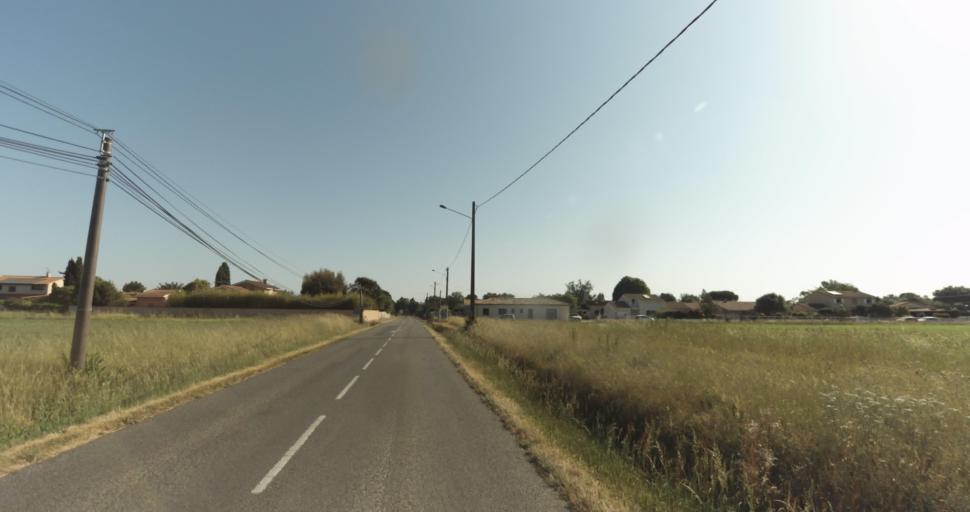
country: FR
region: Midi-Pyrenees
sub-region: Departement de la Haute-Garonne
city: Plaisance-du-Touch
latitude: 43.5522
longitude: 1.2942
